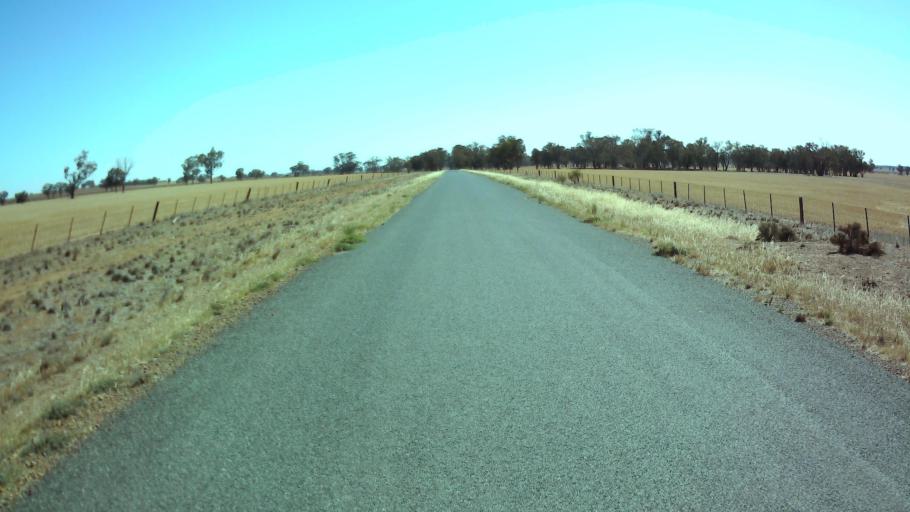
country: AU
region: New South Wales
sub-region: Weddin
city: Grenfell
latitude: -33.7357
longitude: 147.8847
